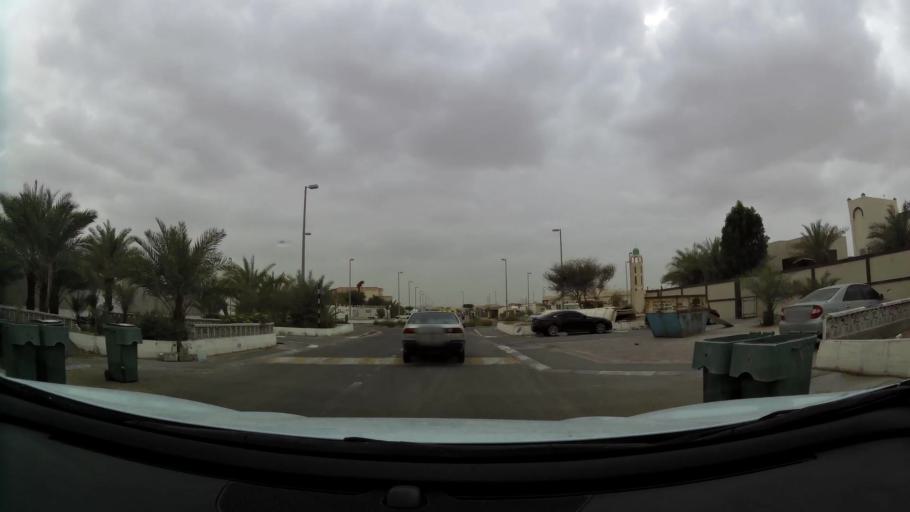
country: AE
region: Abu Dhabi
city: Abu Dhabi
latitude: 24.3313
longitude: 54.6371
